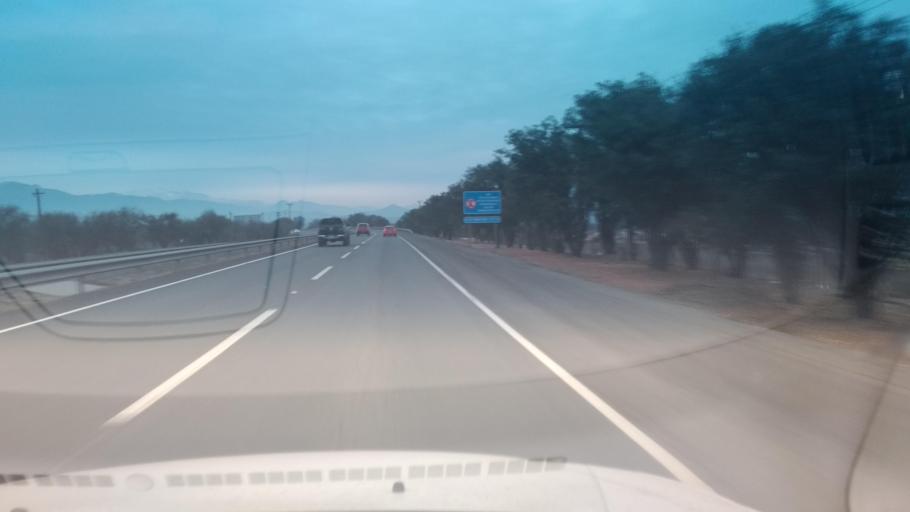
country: CL
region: Santiago Metropolitan
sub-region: Provincia de Chacabuco
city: Chicureo Abajo
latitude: -33.1060
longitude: -70.6900
